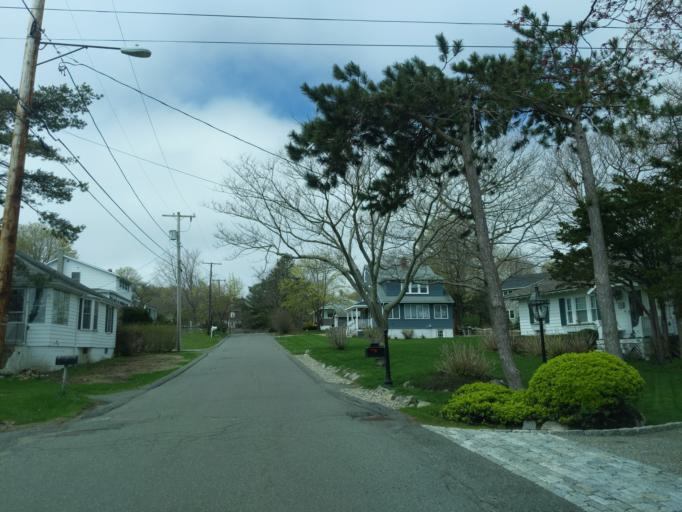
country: US
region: Massachusetts
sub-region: Essex County
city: Rockport
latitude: 42.6482
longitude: -70.5972
